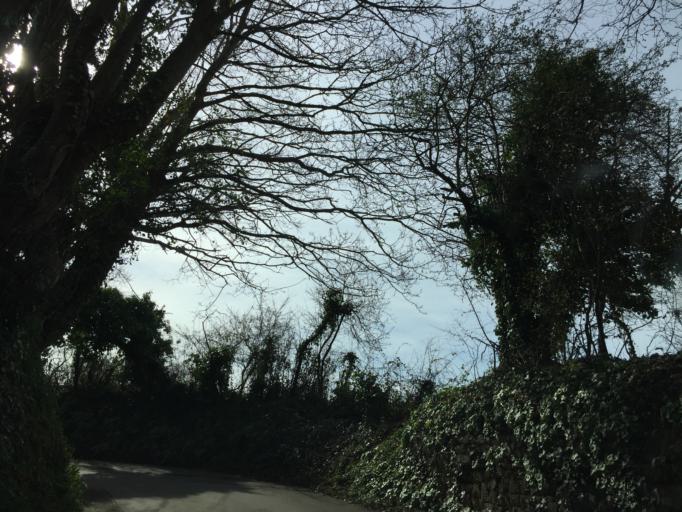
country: JE
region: St Helier
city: Saint Helier
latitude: 49.2189
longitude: -2.1453
